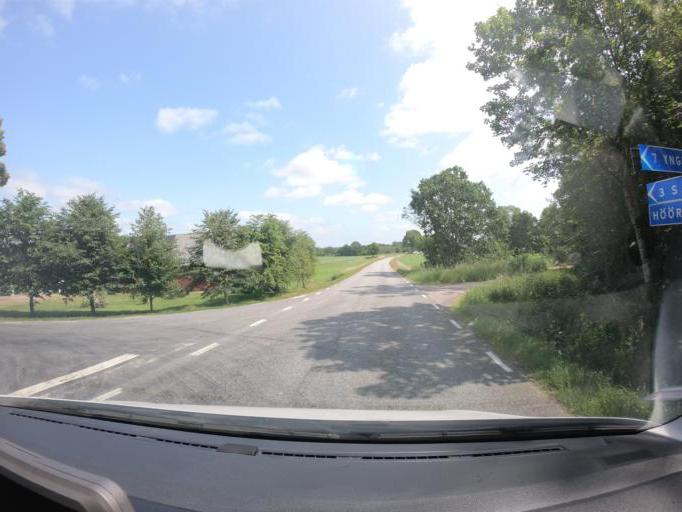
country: SE
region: Skane
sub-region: Horby Kommun
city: Hoerby
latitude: 55.9426
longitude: 13.6434
